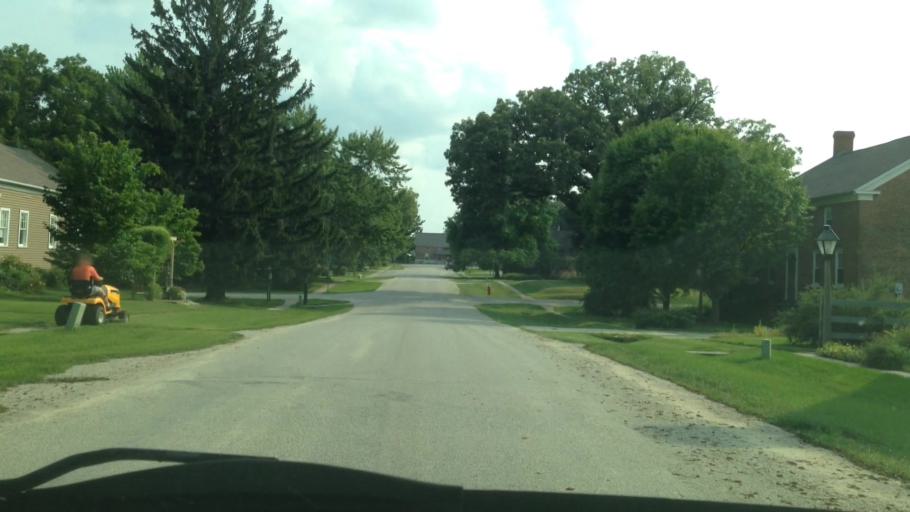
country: US
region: Iowa
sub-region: Benton County
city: Walford
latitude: 41.7965
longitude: -91.9024
